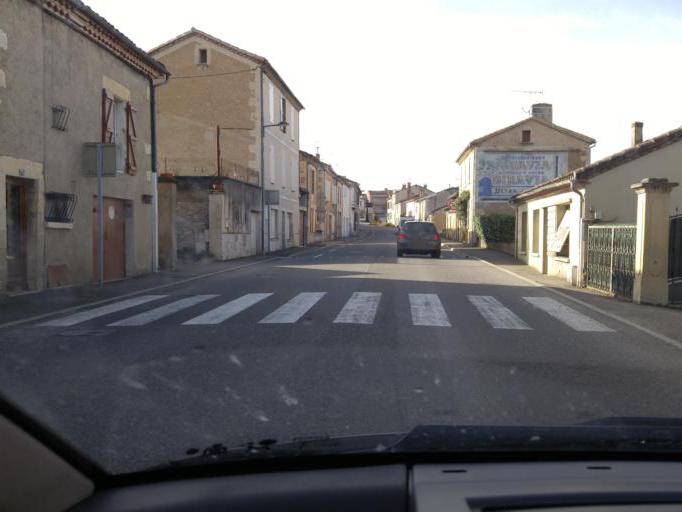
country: FR
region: Midi-Pyrenees
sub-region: Departement du Gers
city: Lectoure
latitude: 43.9338
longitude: 0.6318
